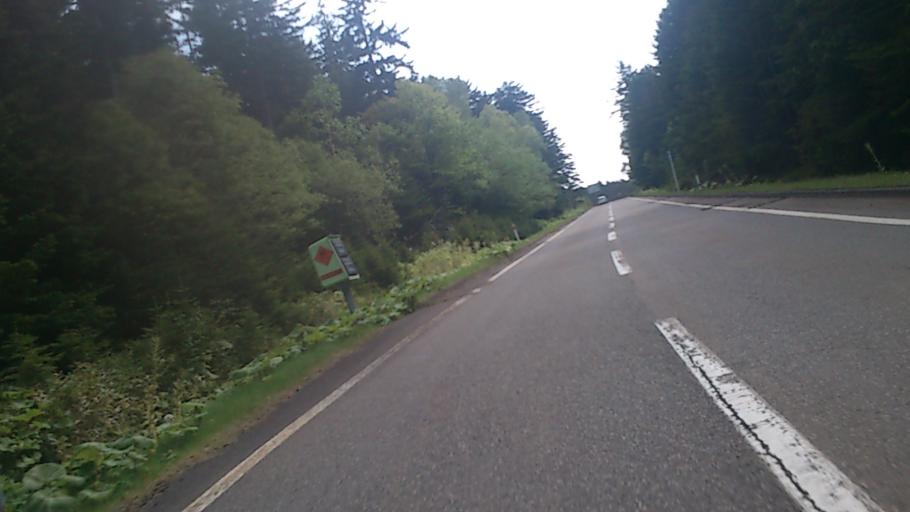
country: JP
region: Hokkaido
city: Kitami
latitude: 43.3978
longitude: 143.9867
